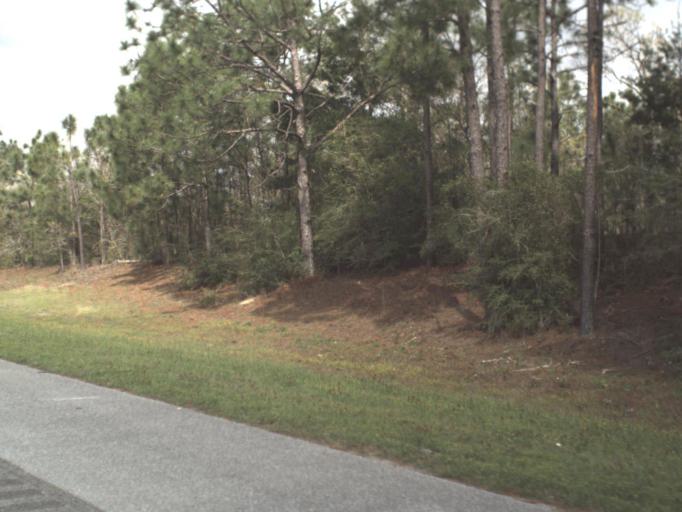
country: US
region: Florida
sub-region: Okaloosa County
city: Crestview
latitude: 30.7269
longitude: -86.5001
